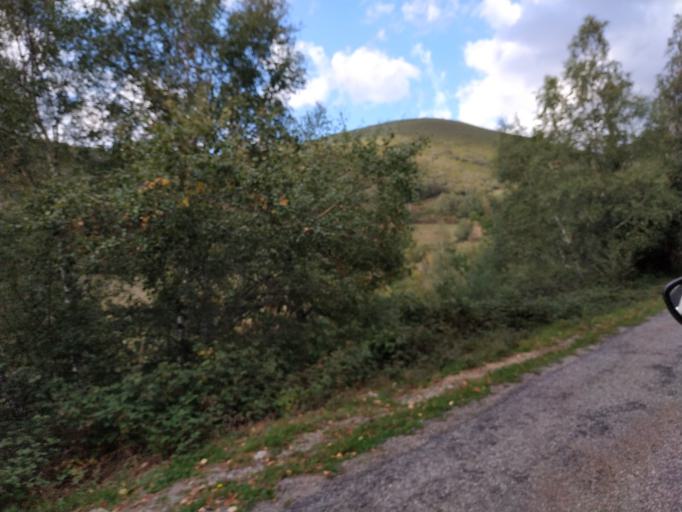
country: ES
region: Castille and Leon
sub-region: Provincia de Leon
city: Candin
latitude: 42.8661
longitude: -6.8463
